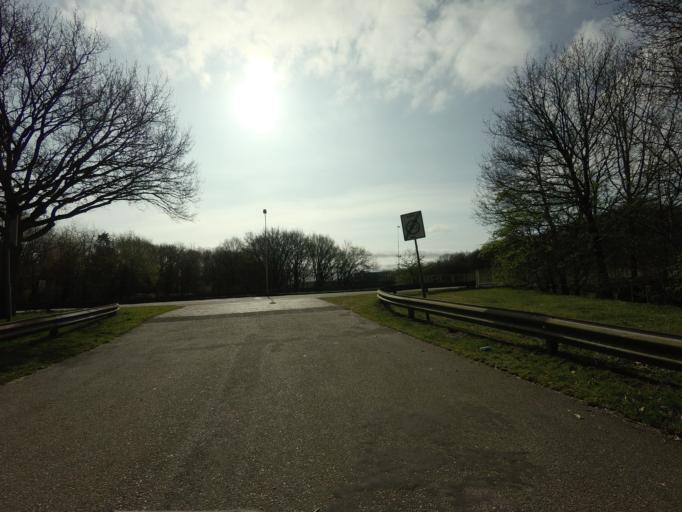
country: NL
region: North Holland
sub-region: Gemeente Laren
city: Laren
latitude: 52.2433
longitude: 5.2211
